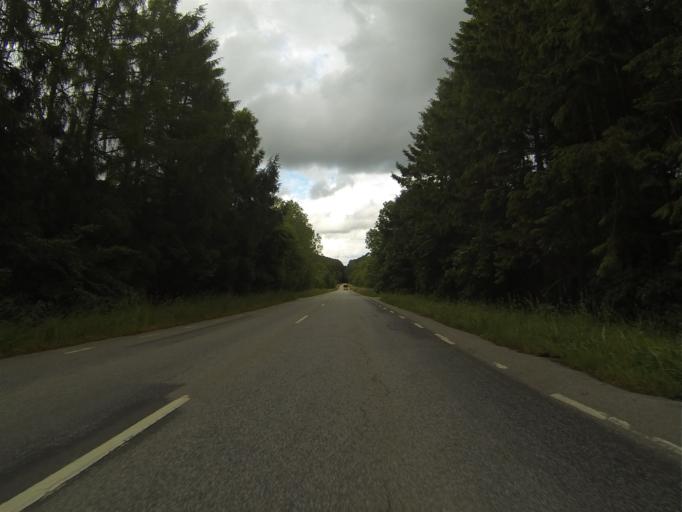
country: SE
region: Skane
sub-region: Lunds Kommun
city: Genarp
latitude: 55.6697
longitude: 13.3984
